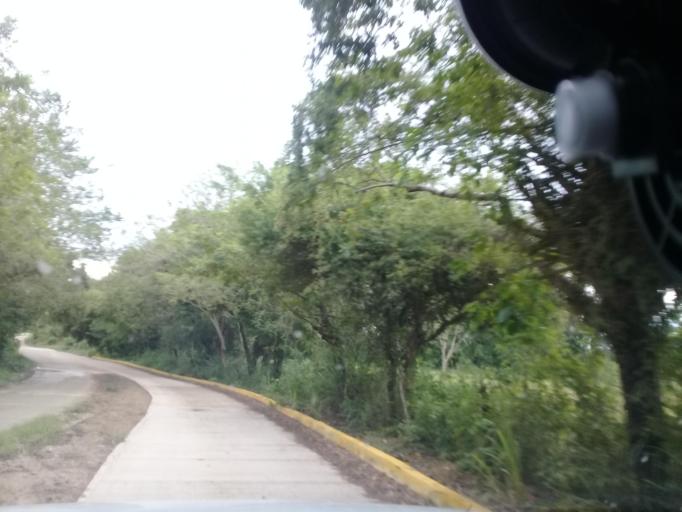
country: MX
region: Hidalgo
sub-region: Huejutla de Reyes
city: Chalahuiyapa
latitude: 21.1630
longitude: -98.3580
